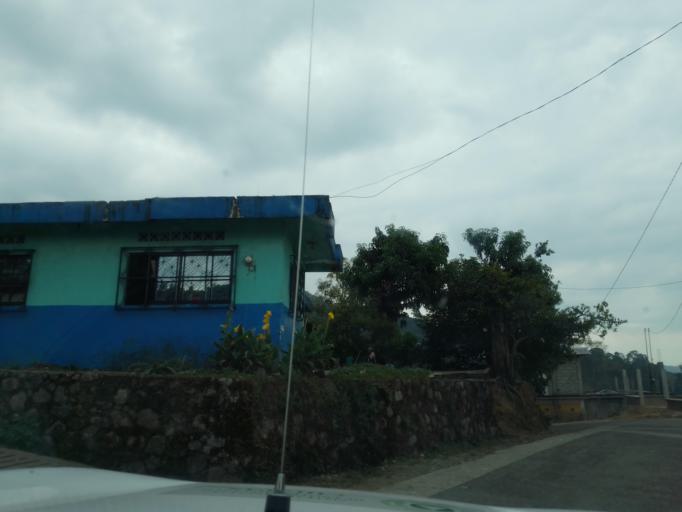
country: MX
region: Chiapas
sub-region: Union Juarez
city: Santo Domingo
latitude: 15.0529
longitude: -92.1230
